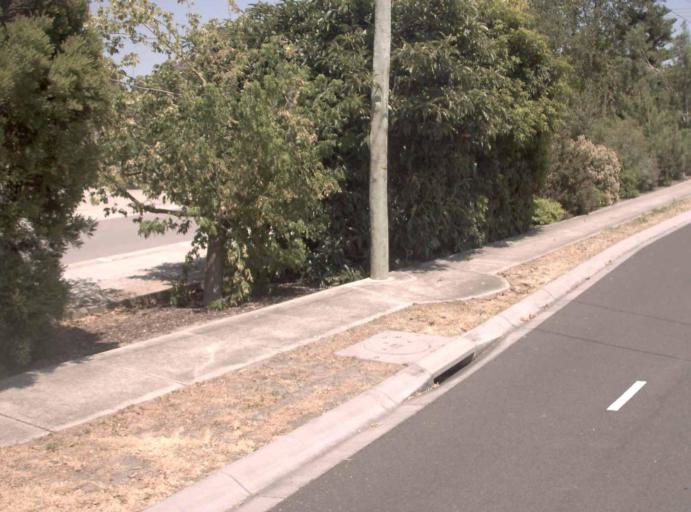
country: AU
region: Victoria
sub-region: Manningham
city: Templestowe Lower
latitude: -37.7678
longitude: 145.1038
